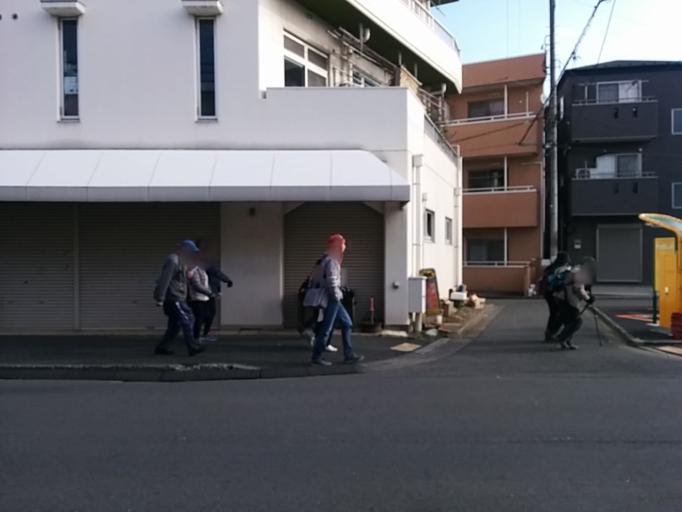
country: JP
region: Saitama
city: Kawagoe
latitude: 35.9055
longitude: 139.4863
